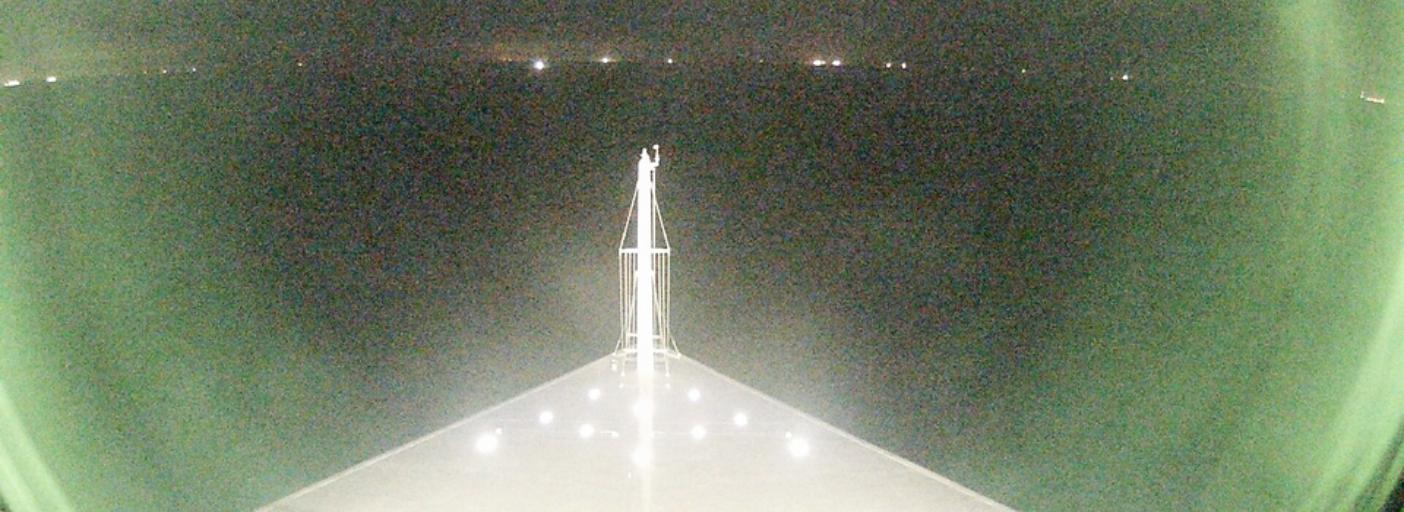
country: DE
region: Schleswig-Holstein
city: Helgoland
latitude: 54.0244
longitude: 7.9150
